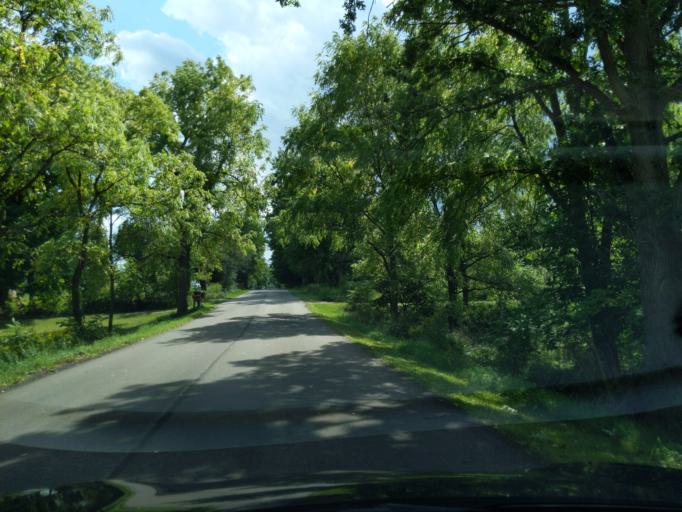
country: US
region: Michigan
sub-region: Eaton County
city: Eaton Rapids
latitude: 42.4725
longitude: -84.5806
